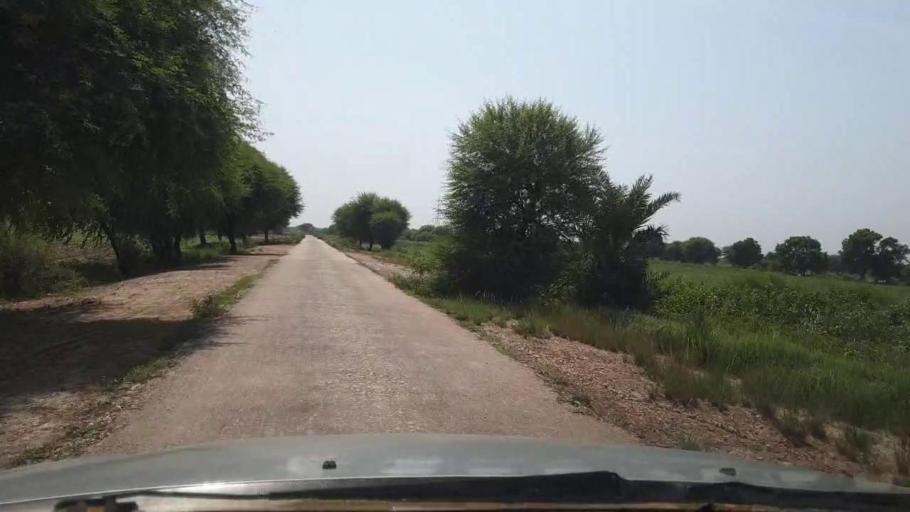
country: PK
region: Sindh
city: Chambar
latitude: 25.2265
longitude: 68.7776
